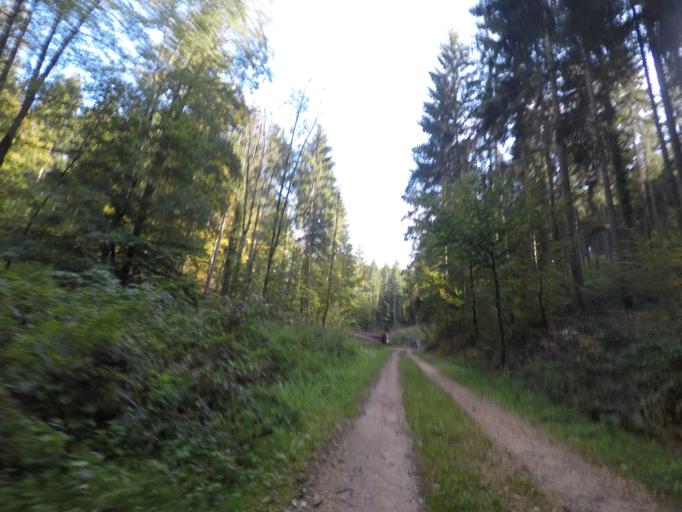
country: LU
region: Luxembourg
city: Itzig
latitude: 49.6074
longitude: 6.1776
